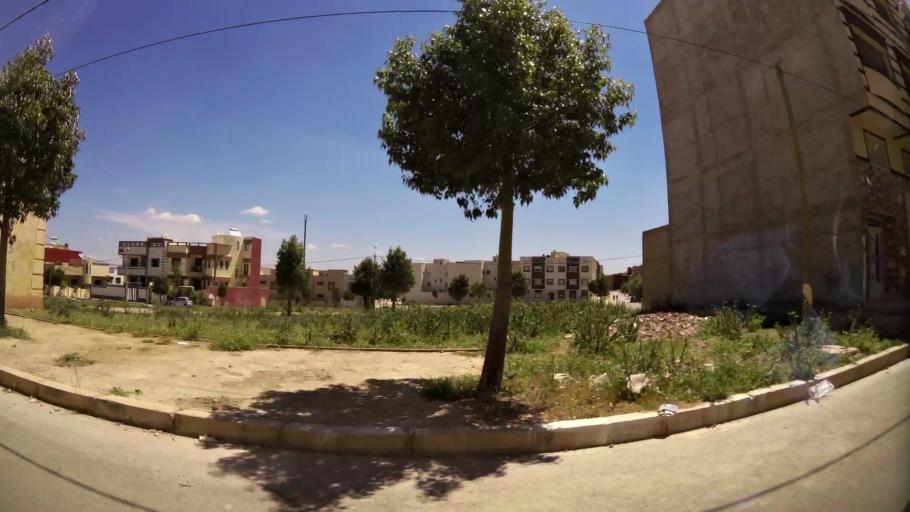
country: MA
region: Oriental
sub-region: Oujda-Angad
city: Oujda
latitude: 34.6575
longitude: -1.9448
